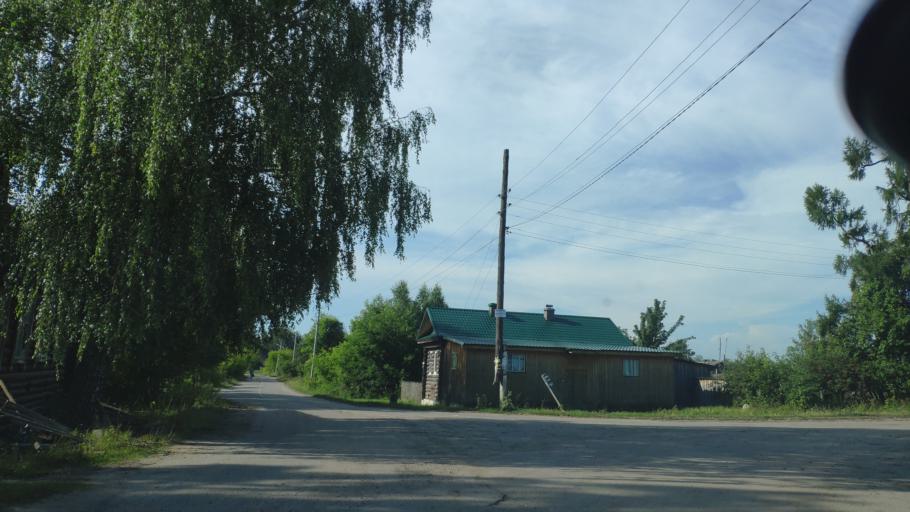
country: RU
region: Nizjnij Novgorod
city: Vorotynets
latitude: 56.1888
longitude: 45.7847
